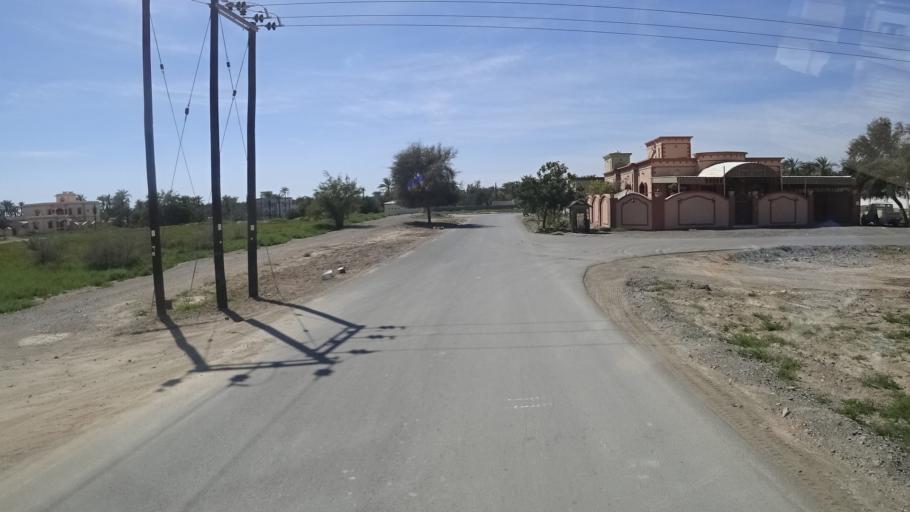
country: OM
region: Al Batinah
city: Al Sohar
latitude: 24.2970
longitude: 56.7957
